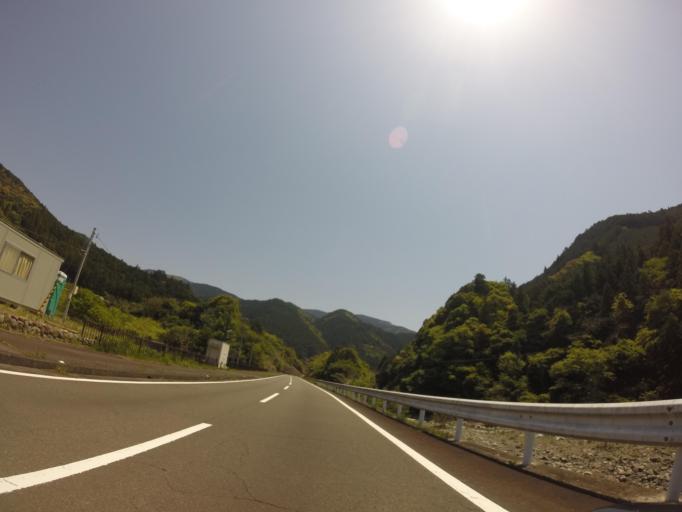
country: JP
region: Shizuoka
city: Shizuoka-shi
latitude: 35.0910
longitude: 138.2388
